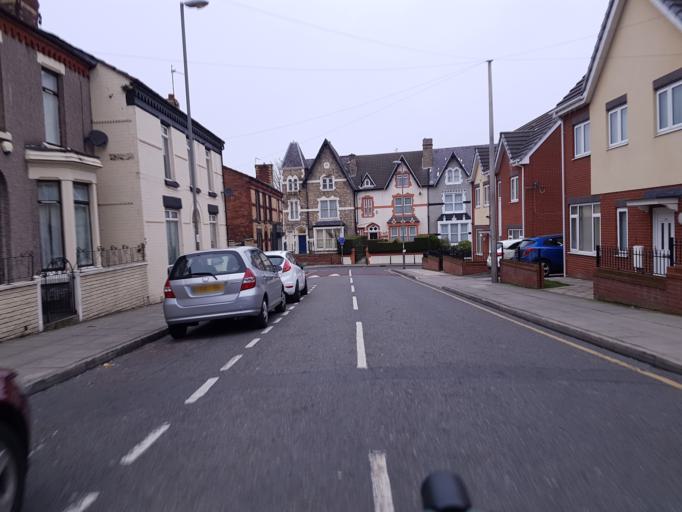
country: GB
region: England
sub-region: Liverpool
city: Liverpool
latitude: 53.4436
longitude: -2.9644
